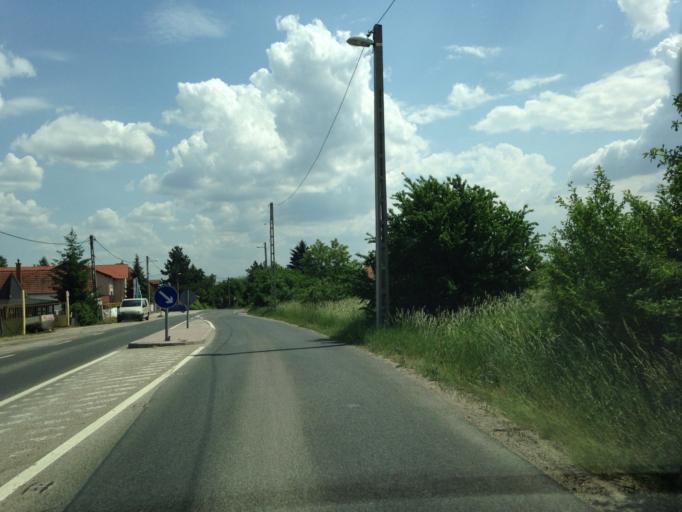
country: HU
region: Pest
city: Szentendre
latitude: 47.6839
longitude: 19.0606
